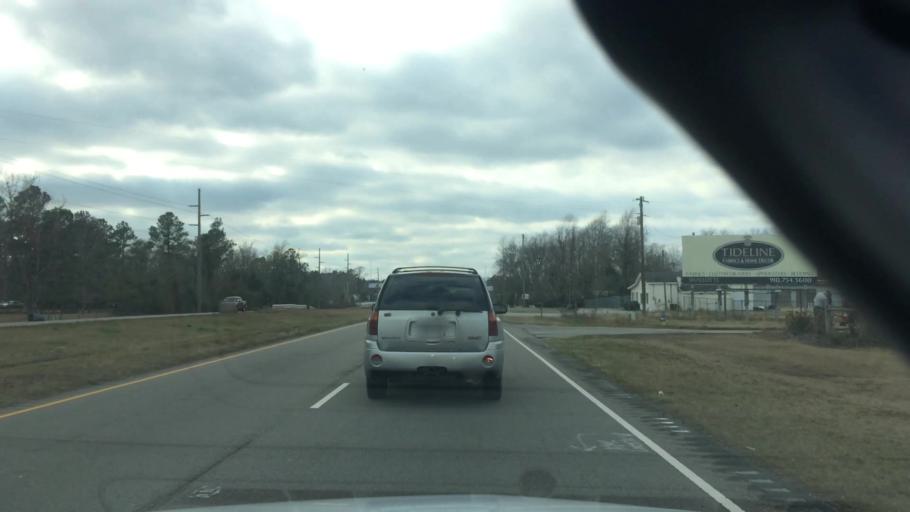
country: US
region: North Carolina
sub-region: Brunswick County
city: Shallotte
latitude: 34.0101
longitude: -78.2938
